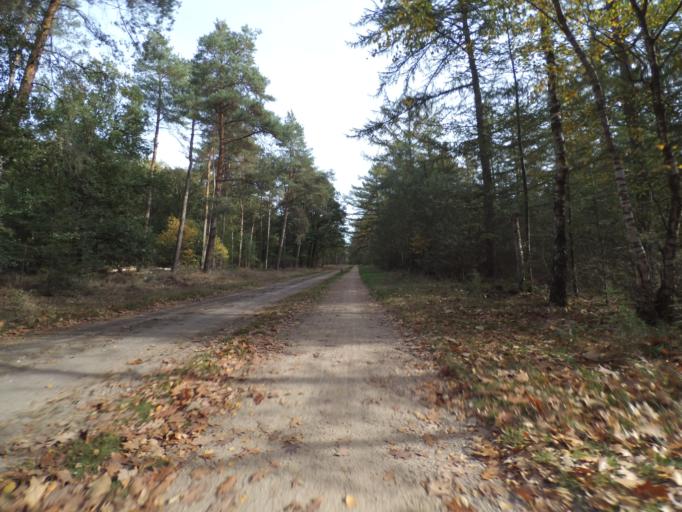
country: NL
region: Overijssel
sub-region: Gemeente Raalte
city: Raalte
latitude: 52.3538
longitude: 6.3923
